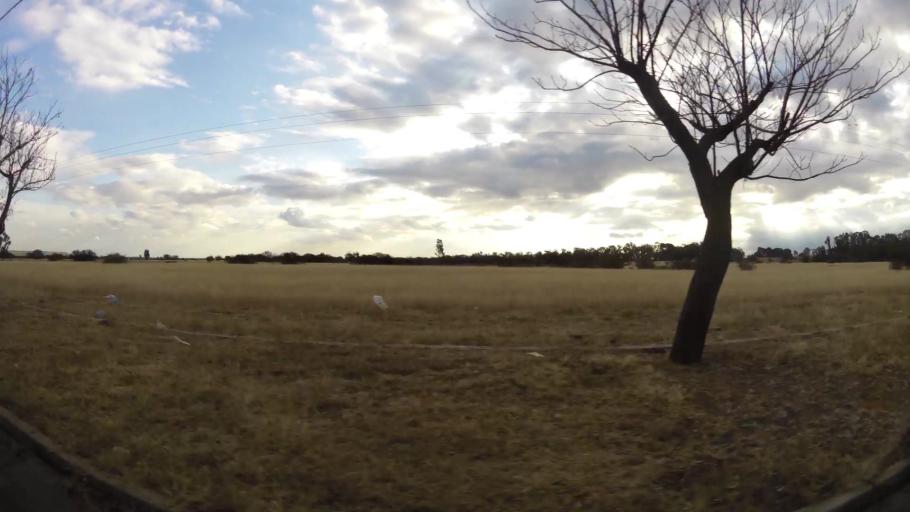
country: ZA
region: Orange Free State
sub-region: Lejweleputswa District Municipality
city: Welkom
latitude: -28.0018
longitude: 26.7106
